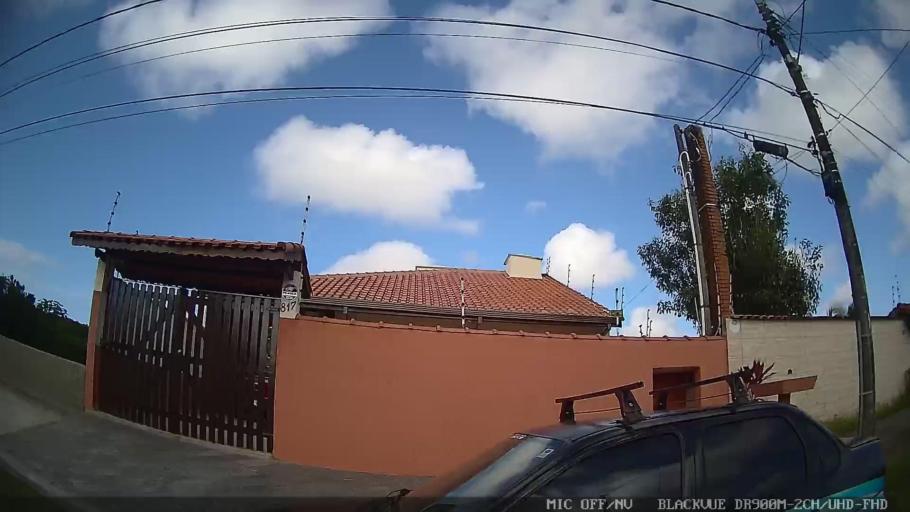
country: BR
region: Sao Paulo
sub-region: Peruibe
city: Peruibe
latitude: -24.2695
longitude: -46.9421
